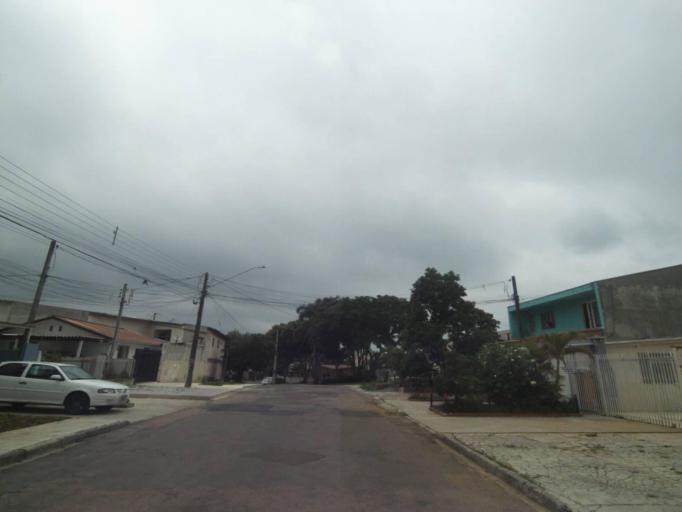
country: BR
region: Parana
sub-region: Curitiba
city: Curitiba
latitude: -25.4840
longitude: -49.3544
